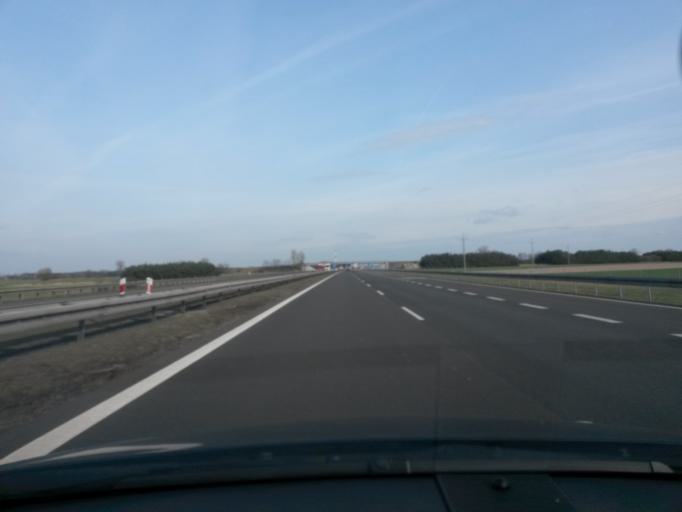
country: PL
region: Greater Poland Voivodeship
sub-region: Powiat slupecki
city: Ladek
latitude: 52.2259
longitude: 17.9344
